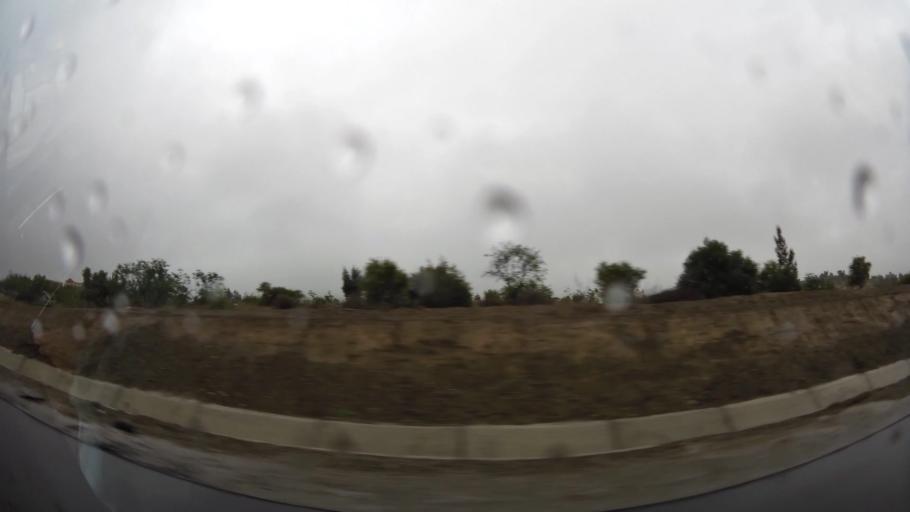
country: MA
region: Oriental
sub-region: Nador
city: Midar
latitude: 34.8614
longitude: -3.7230
